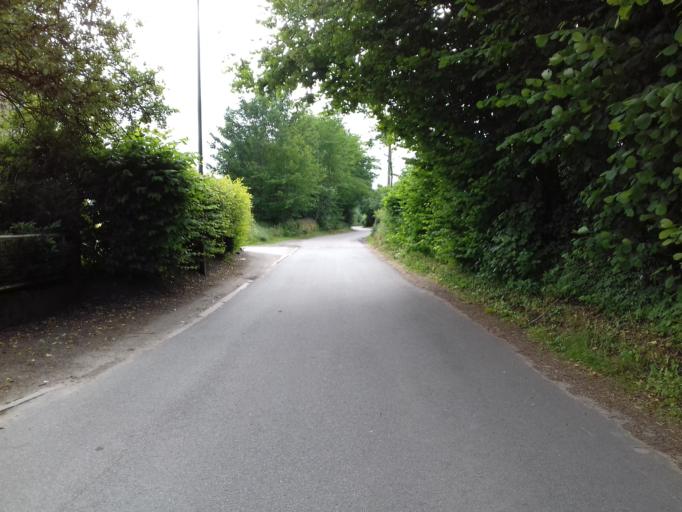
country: DE
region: Schleswig-Holstein
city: Tasdorf
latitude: 54.0774
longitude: 10.0148
